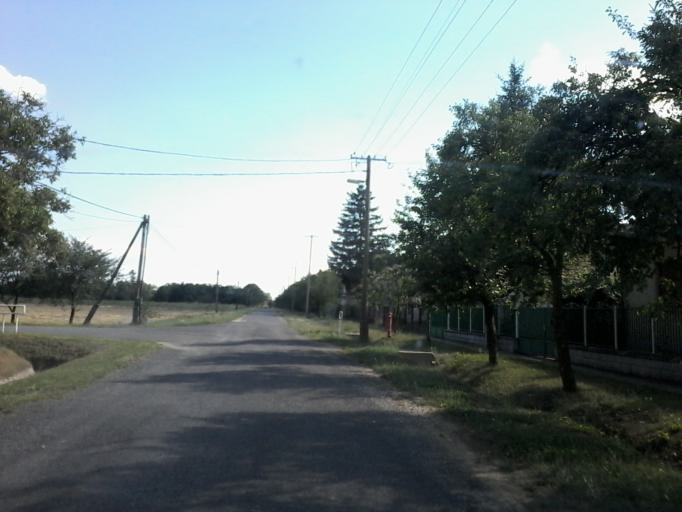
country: HU
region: Vas
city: Janoshaza
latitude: 47.0570
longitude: 17.1352
